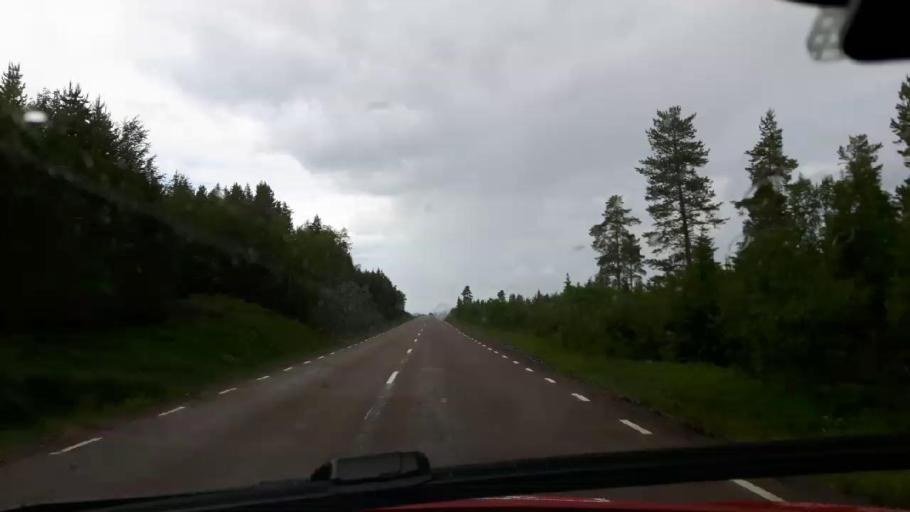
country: SE
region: Jaemtland
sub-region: Krokoms Kommun
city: Krokom
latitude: 63.8850
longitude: 14.2827
